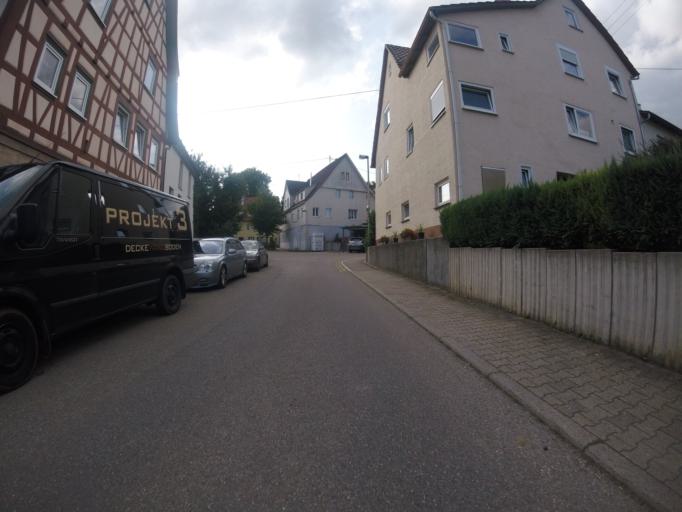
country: DE
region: Baden-Wuerttemberg
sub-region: Regierungsbezirk Stuttgart
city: Aspach
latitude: 48.9881
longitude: 9.4079
